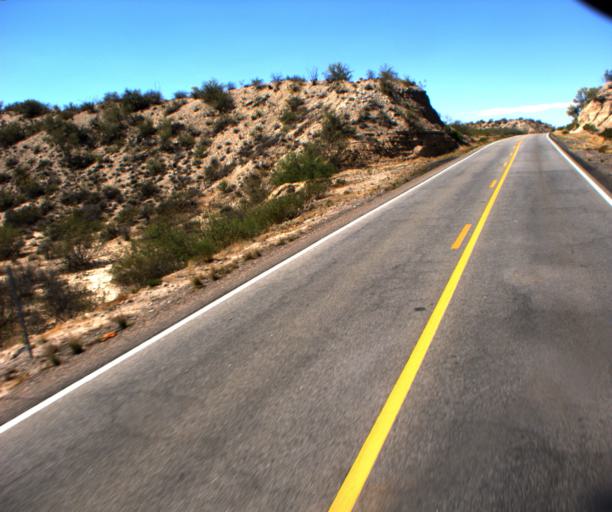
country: US
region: Arizona
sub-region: Yavapai County
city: Bagdad
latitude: 34.7760
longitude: -113.6221
